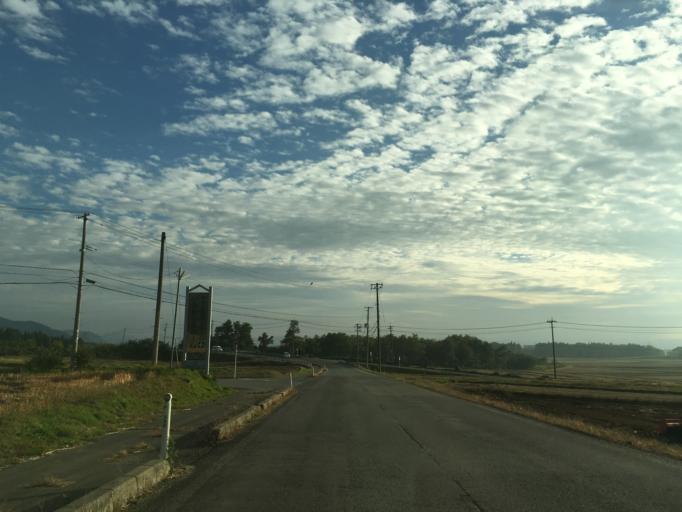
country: JP
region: Fukushima
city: Inawashiro
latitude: 37.5632
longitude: 140.1341
